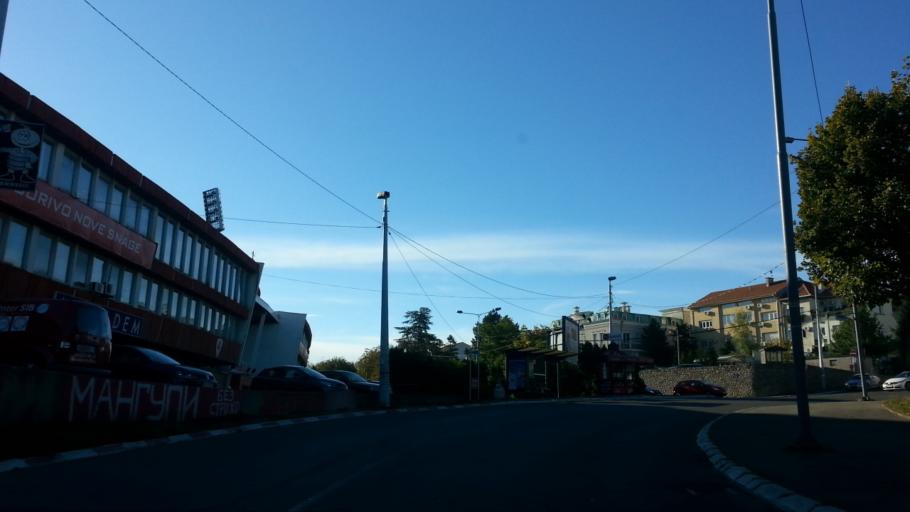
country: RS
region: Central Serbia
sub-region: Belgrade
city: Savski Venac
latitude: 44.7834
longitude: 20.4629
